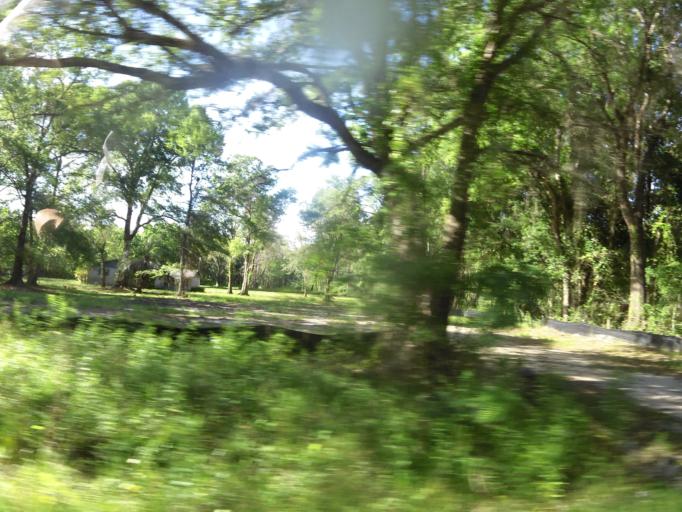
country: US
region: Florida
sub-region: Nassau County
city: Nassau Village-Ratliff
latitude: 30.5106
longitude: -81.7892
